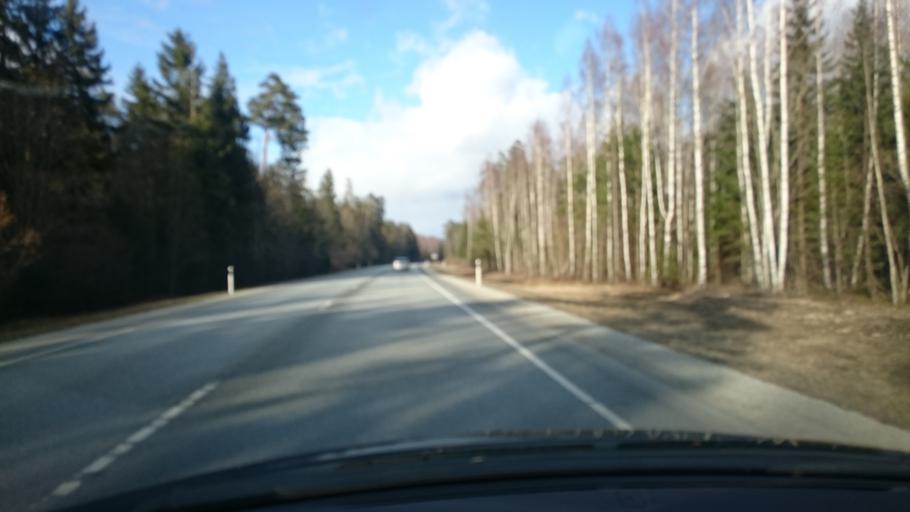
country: EE
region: Harju
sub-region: Keila linn
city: Keila
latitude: 59.1922
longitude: 24.4033
